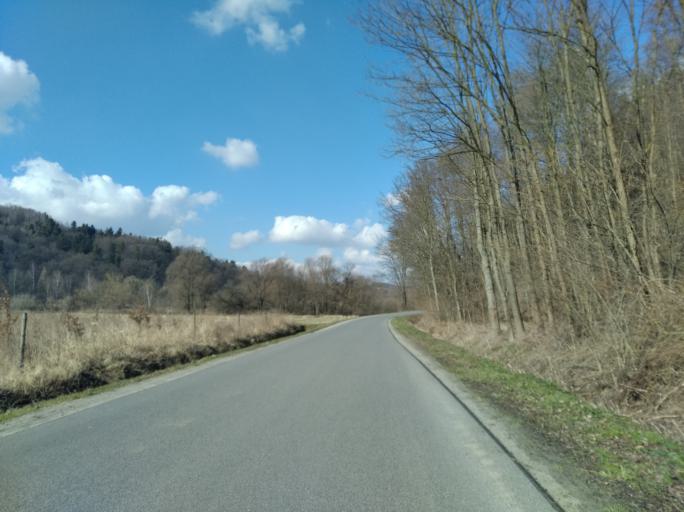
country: PL
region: Subcarpathian Voivodeship
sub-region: Powiat strzyzowski
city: Frysztak
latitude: 49.8509
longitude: 21.6244
